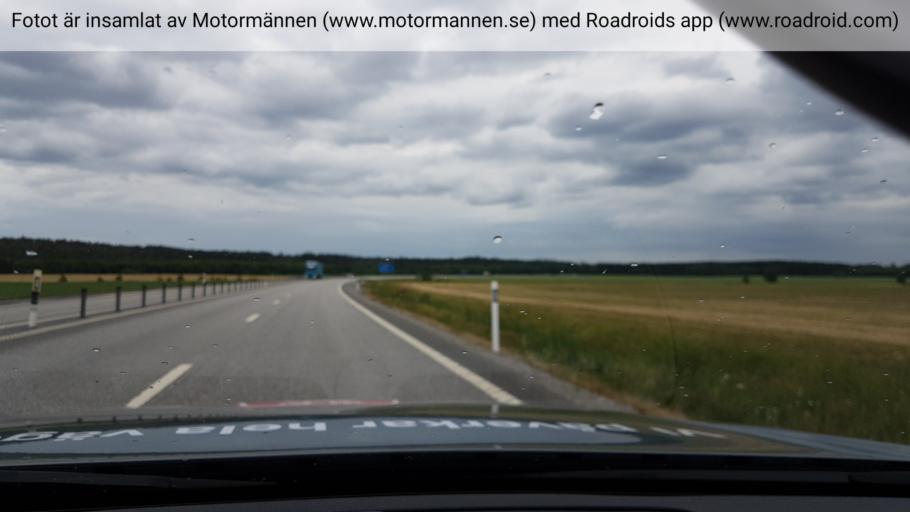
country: SE
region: Vaestmanland
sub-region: Surahammars Kommun
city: Ramnas
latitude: 59.7560
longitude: 16.2178
